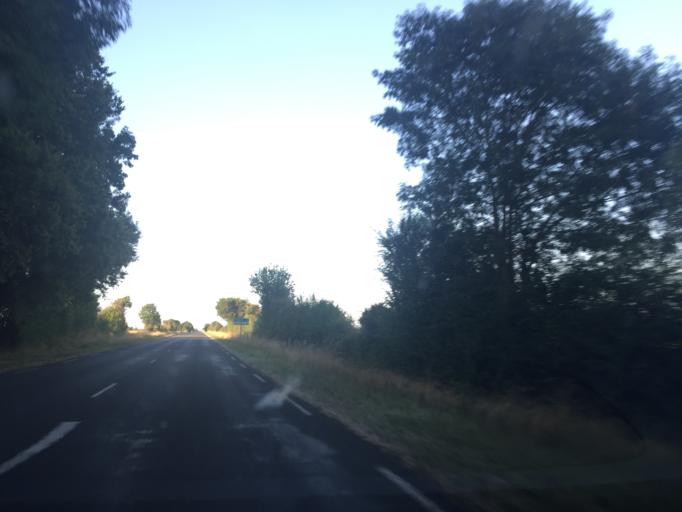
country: FR
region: Poitou-Charentes
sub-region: Departement de la Vienne
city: Saint-Sauvant
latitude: 46.3581
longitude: 0.0152
